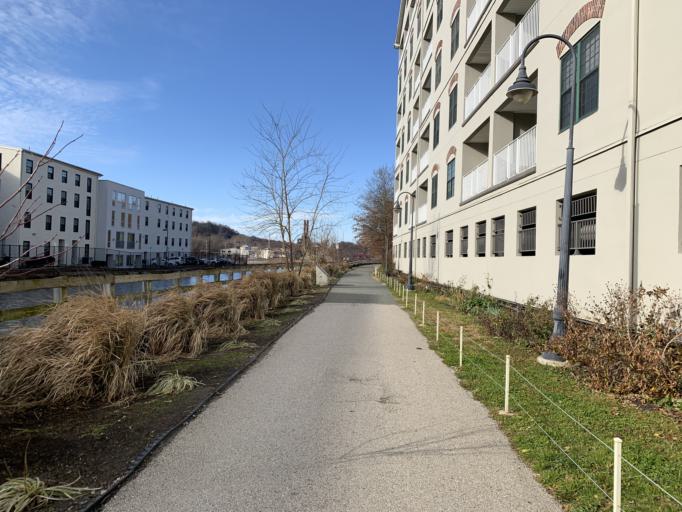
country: US
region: Pennsylvania
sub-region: Montgomery County
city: Bala-Cynwyd
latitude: 40.0293
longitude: -75.2312
